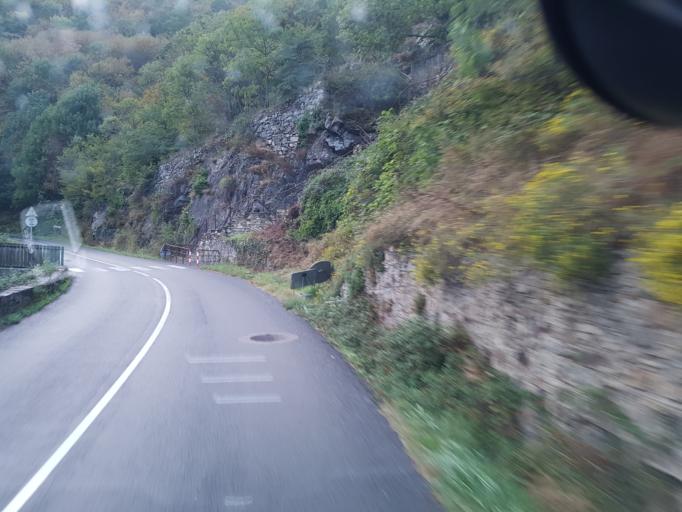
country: FR
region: Midi-Pyrenees
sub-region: Departement du Tarn
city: Mazamet
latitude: 43.4807
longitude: 2.3748
